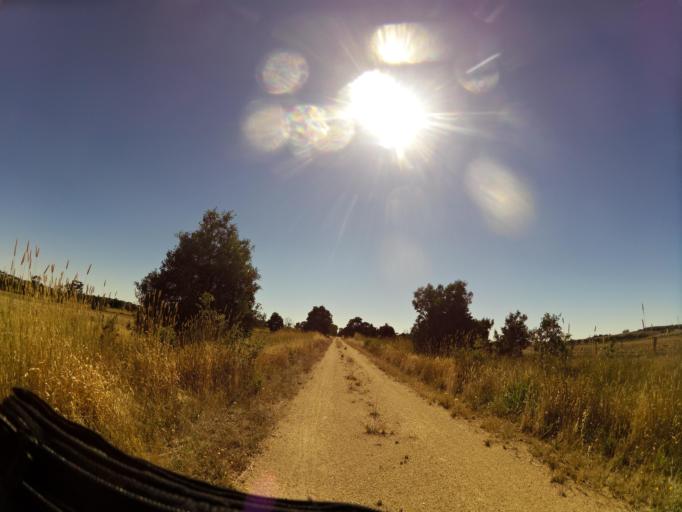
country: AU
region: Victoria
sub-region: Ballarat North
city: Delacombe
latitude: -37.6839
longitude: 143.4157
